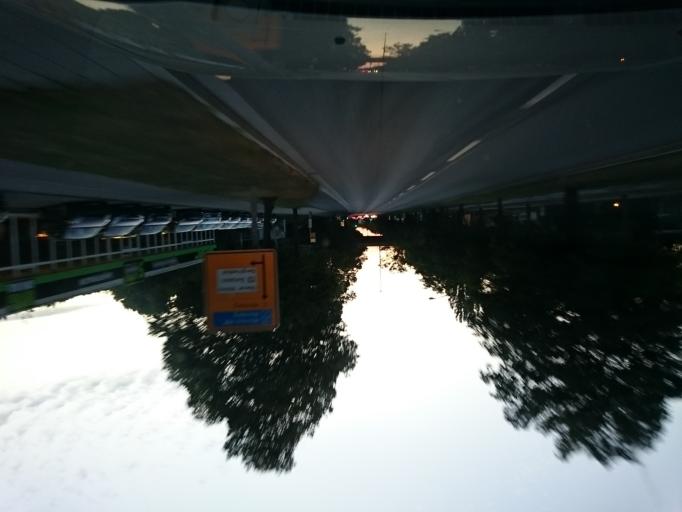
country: DE
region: Bavaria
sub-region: Upper Palatinate
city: Lappersdorf
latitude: 49.0284
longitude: 12.0927
